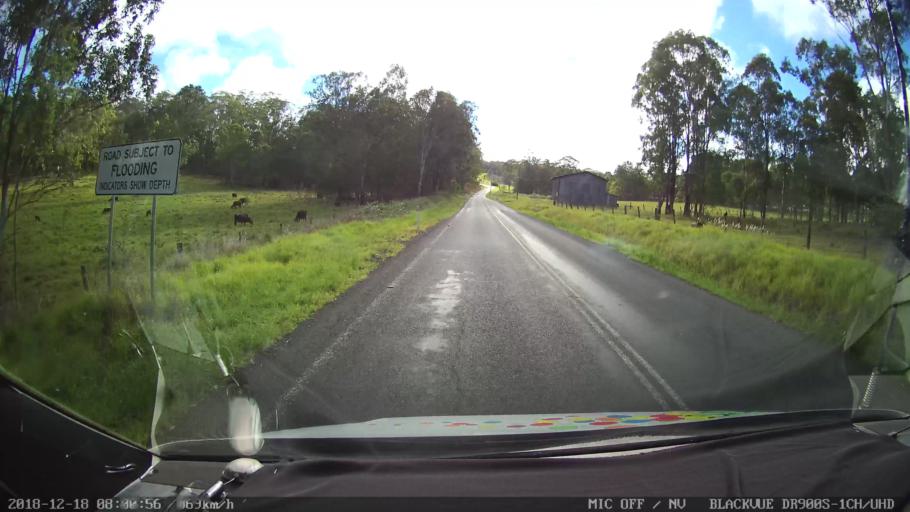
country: AU
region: New South Wales
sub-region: Kyogle
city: Kyogle
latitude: -28.3895
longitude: 152.6173
